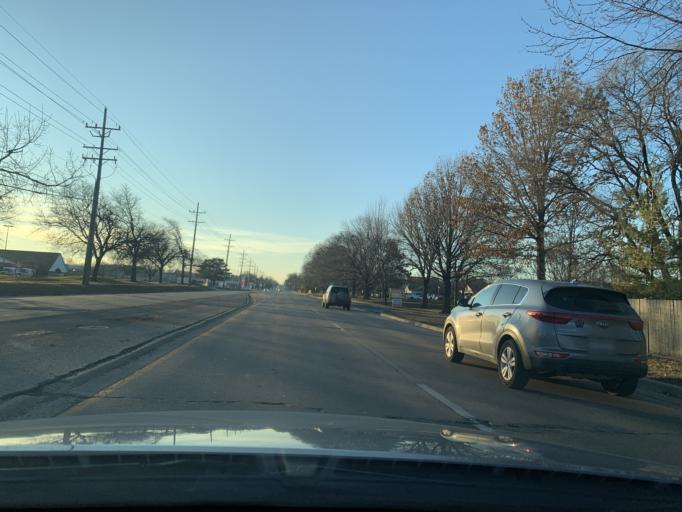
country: US
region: Illinois
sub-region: DuPage County
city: Roselle
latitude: 41.9990
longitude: -88.0554
